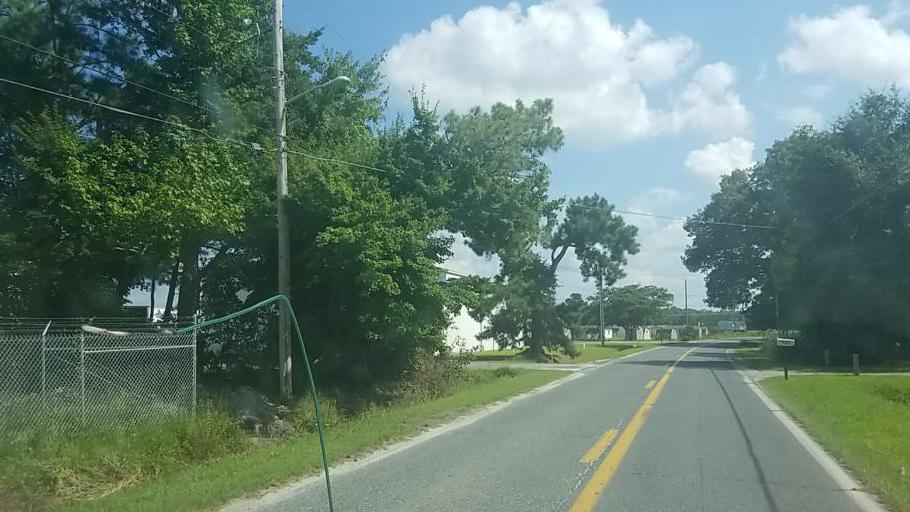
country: US
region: Maryland
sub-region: Wicomico County
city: Fruitland
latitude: 38.3094
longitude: -75.6317
